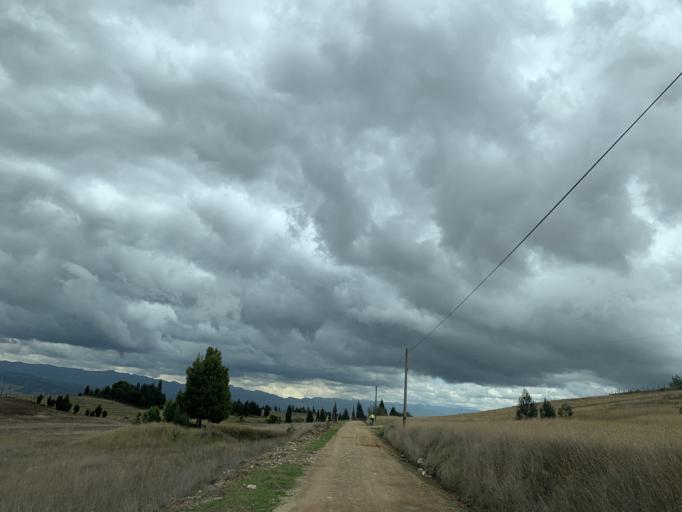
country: CO
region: Boyaca
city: Tunja
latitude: 5.5568
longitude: -73.3152
